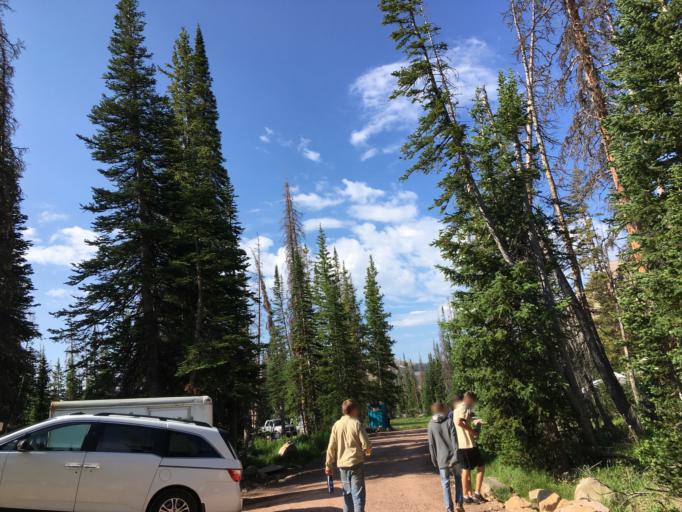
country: US
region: Utah
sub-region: Summit County
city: Kamas
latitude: 40.7197
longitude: -110.8819
